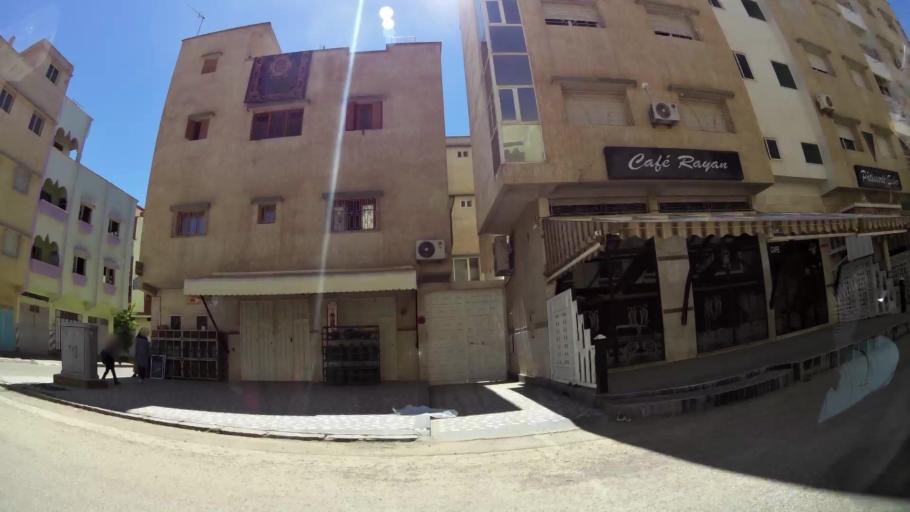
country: MA
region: Meknes-Tafilalet
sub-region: Meknes
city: Meknes
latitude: 33.8947
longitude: -5.5829
